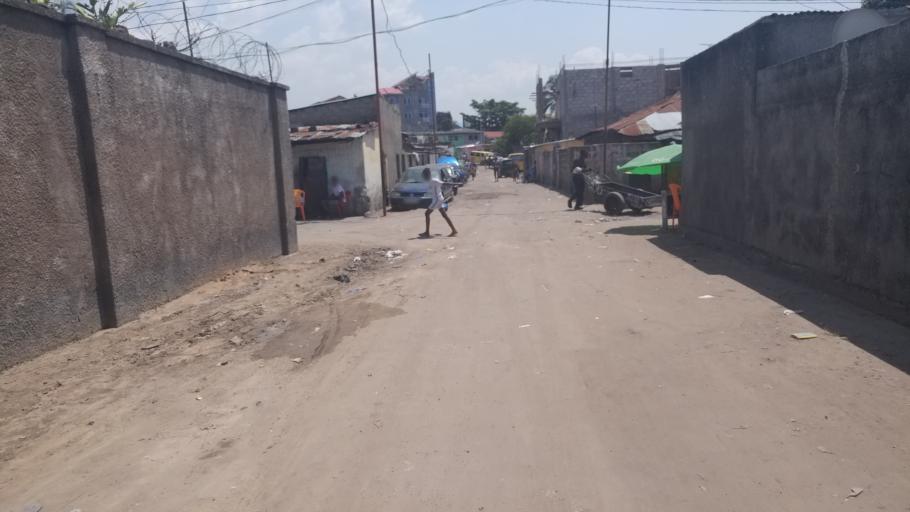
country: CD
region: Kinshasa
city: Kinshasa
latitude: -4.3385
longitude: 15.2614
